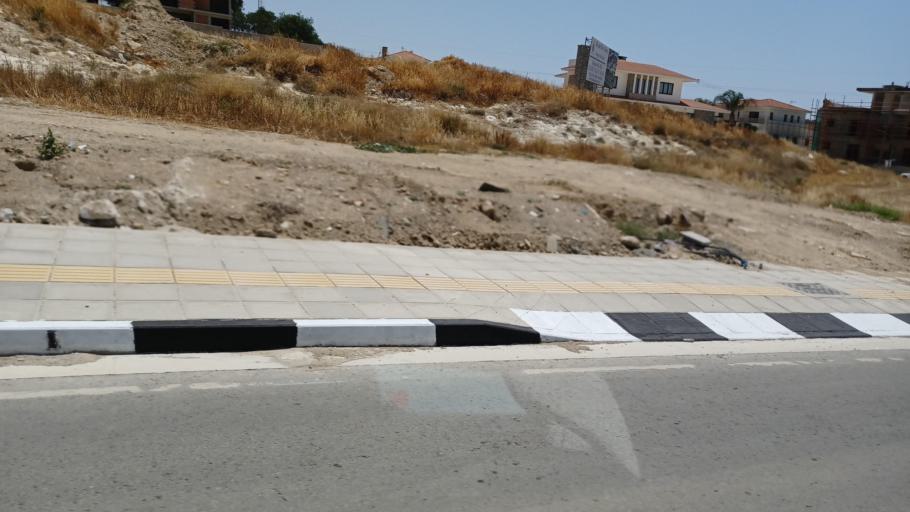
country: CY
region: Larnaka
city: Pyla
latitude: 34.9985
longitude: 33.6919
